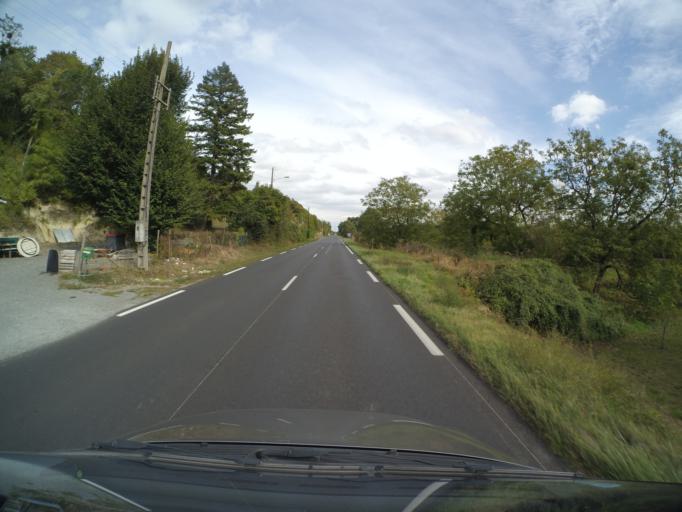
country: FR
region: Centre
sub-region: Departement d'Indre-et-Loire
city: Langeais
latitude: 47.3158
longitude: 0.3829
